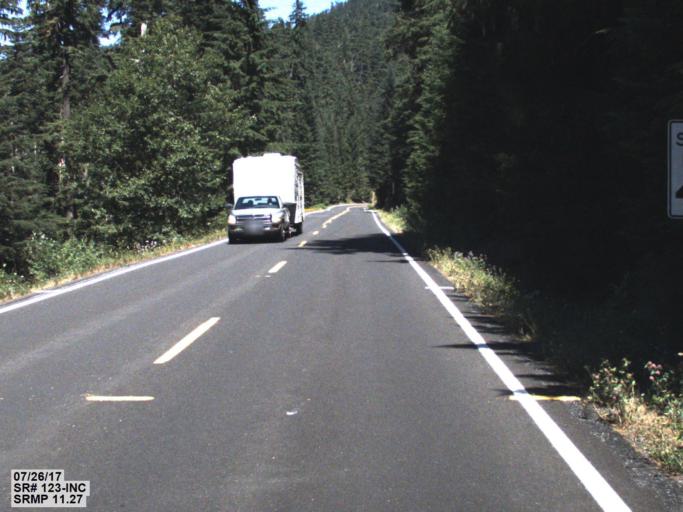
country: US
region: Washington
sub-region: King County
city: Enumclaw
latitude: 46.8319
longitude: -121.5365
